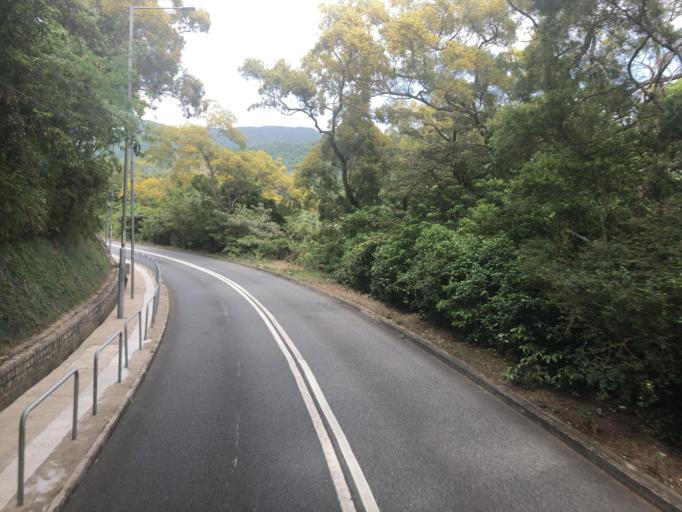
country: HK
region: Sai Kung
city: Sai Kung
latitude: 22.3887
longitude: 114.2942
